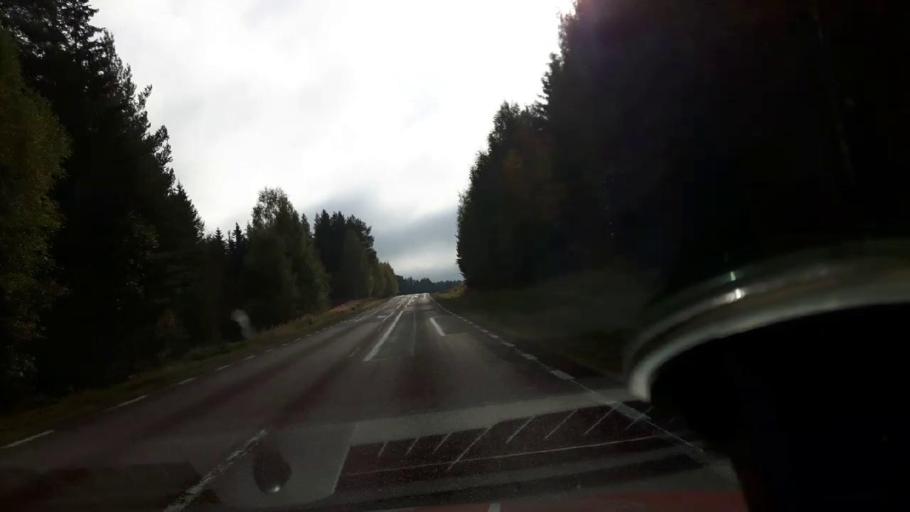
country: SE
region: Gaevleborg
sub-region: Ljusdals Kommun
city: Farila
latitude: 61.8786
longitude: 15.7154
